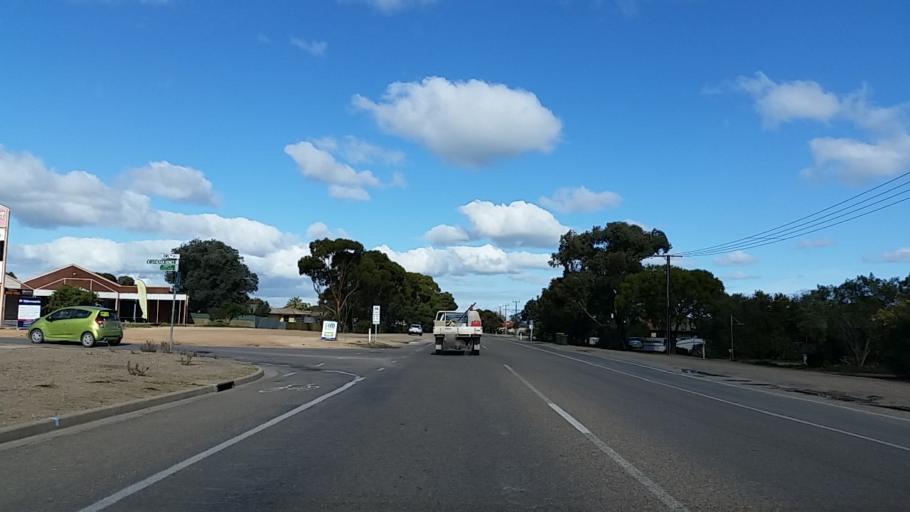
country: AU
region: South Australia
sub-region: Murray Bridge
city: Murray Bridge
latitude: -35.1422
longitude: 139.2856
